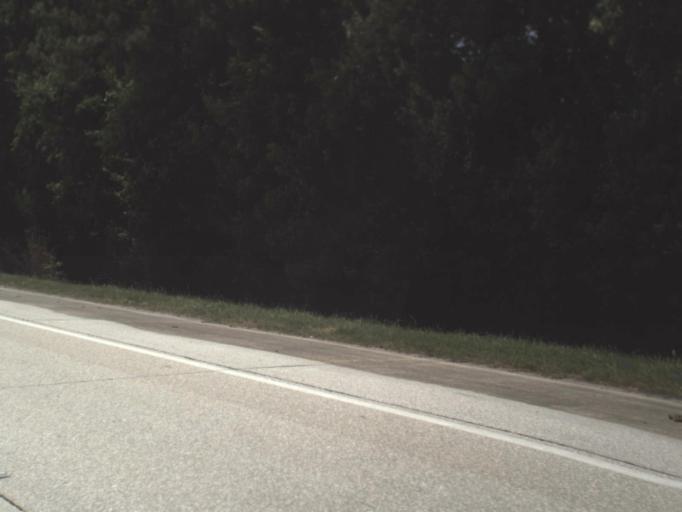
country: US
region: Florida
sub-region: Duval County
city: Jacksonville
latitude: 30.2263
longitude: -81.5750
